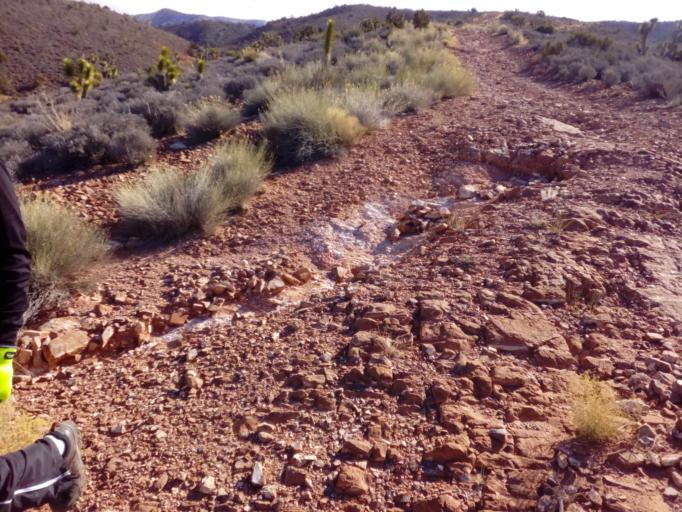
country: US
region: Nevada
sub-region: Clark County
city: Summerlin South
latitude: 36.0799
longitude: -115.5751
